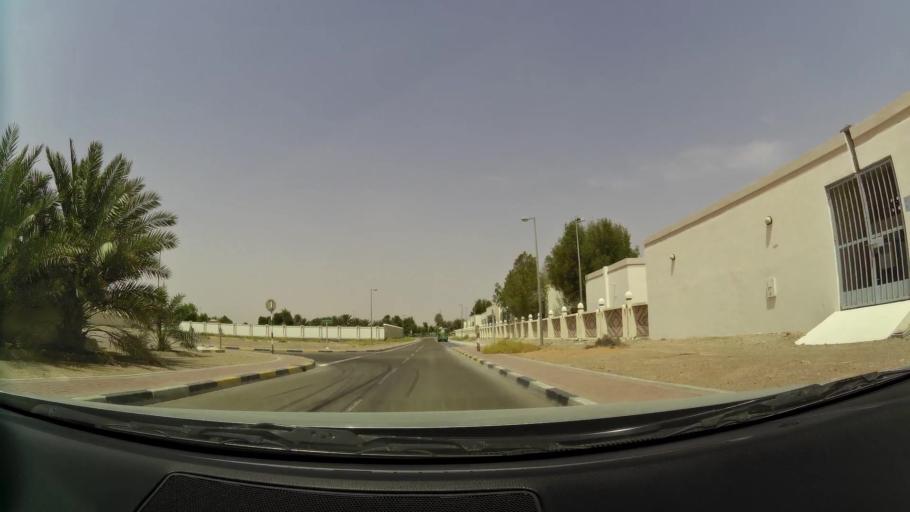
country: AE
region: Abu Dhabi
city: Al Ain
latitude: 24.1784
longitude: 55.7080
